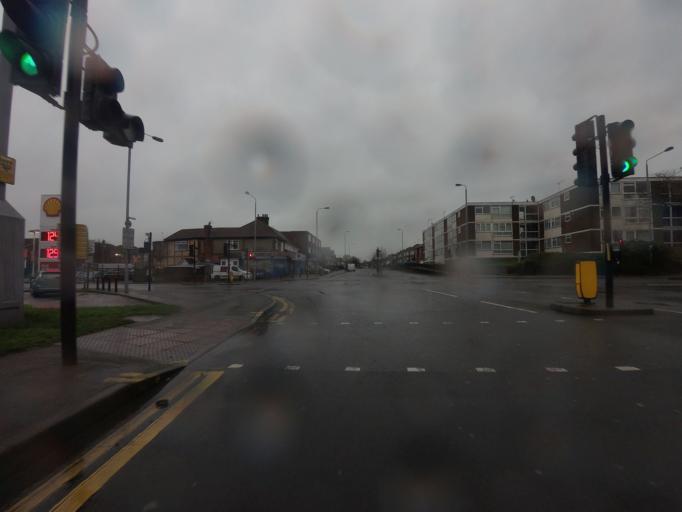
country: GB
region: England
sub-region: Greater London
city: Woodford Green
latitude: 51.6359
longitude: -0.0130
